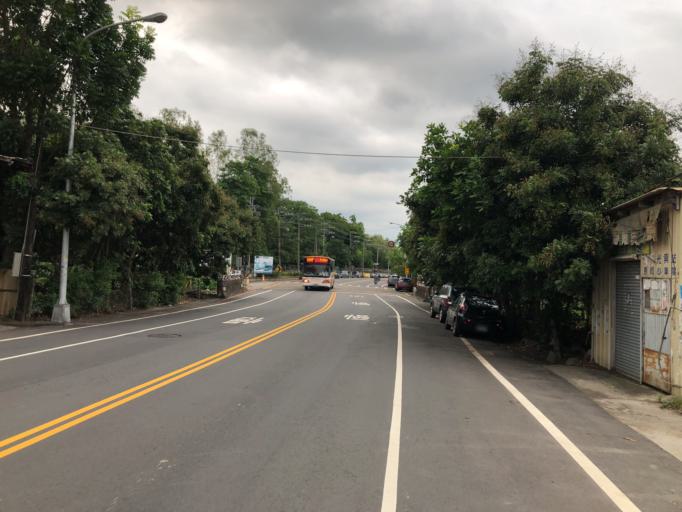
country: TW
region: Taiwan
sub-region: Taichung City
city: Taichung
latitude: 24.1152
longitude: 120.7323
